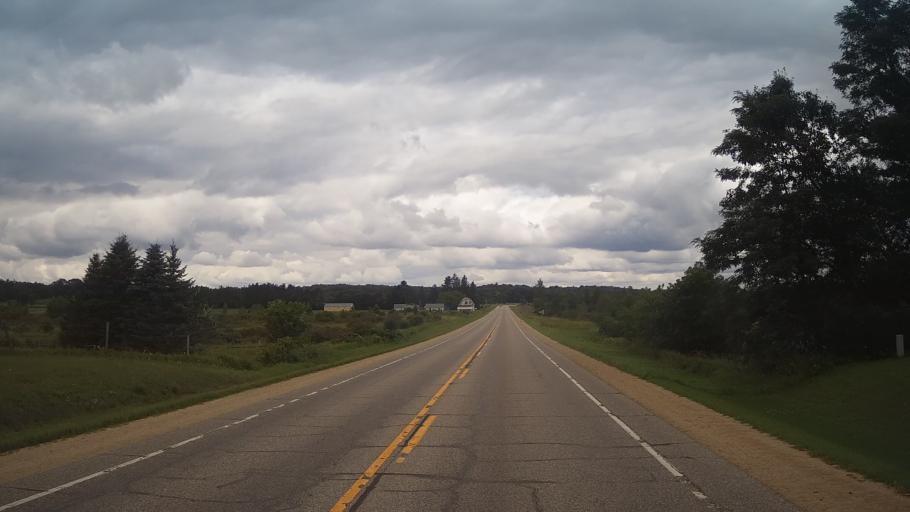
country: US
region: Wisconsin
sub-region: Waushara County
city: Wautoma
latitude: 44.0578
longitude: -89.3653
